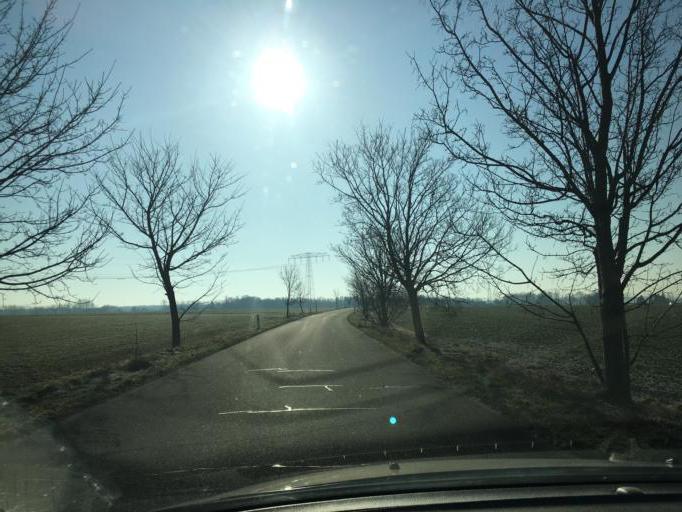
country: DE
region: Saxony
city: Belgershain
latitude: 51.2232
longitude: 12.5557
